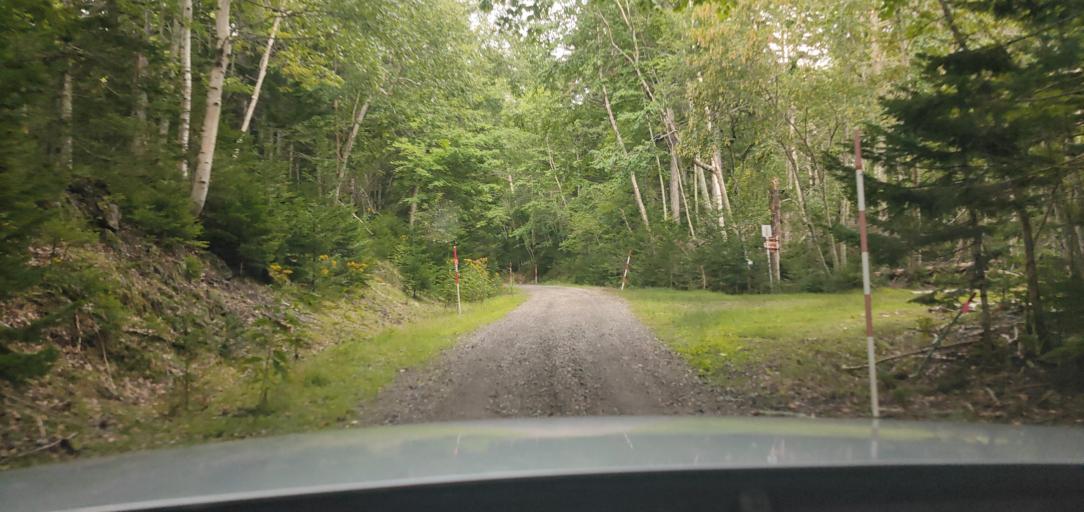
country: JP
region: Hokkaido
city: Kitami
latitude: 43.3695
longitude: 143.9510
